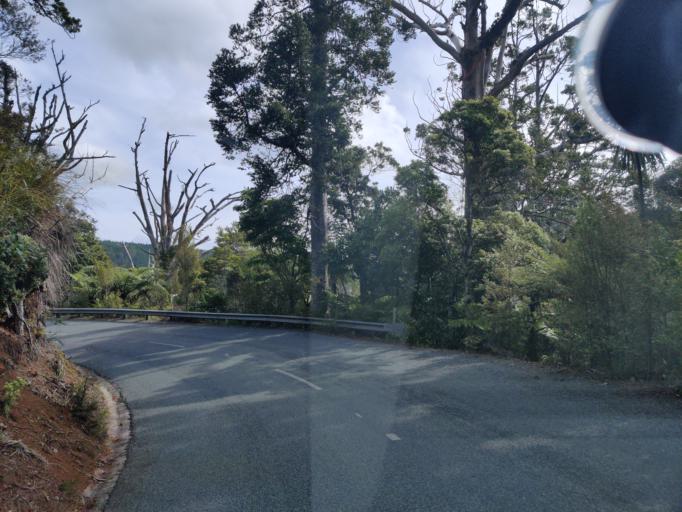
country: NZ
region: Northland
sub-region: Kaipara District
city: Dargaville
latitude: -35.6461
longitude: 173.5576
